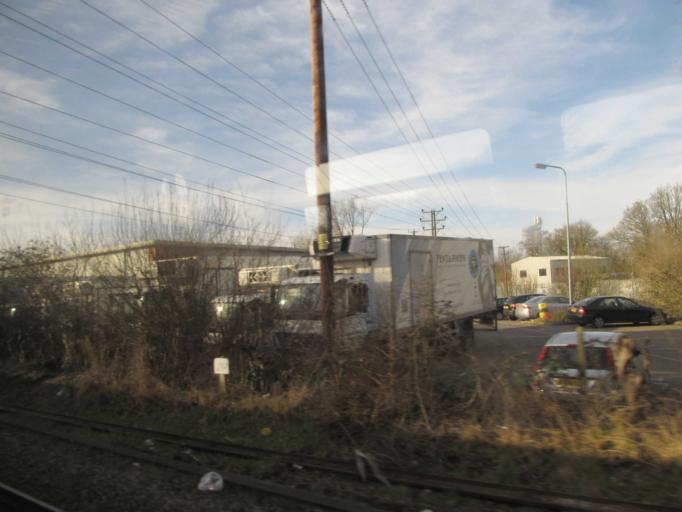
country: GB
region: England
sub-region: Hampshire
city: Farnborough
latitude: 51.2783
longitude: -0.7322
